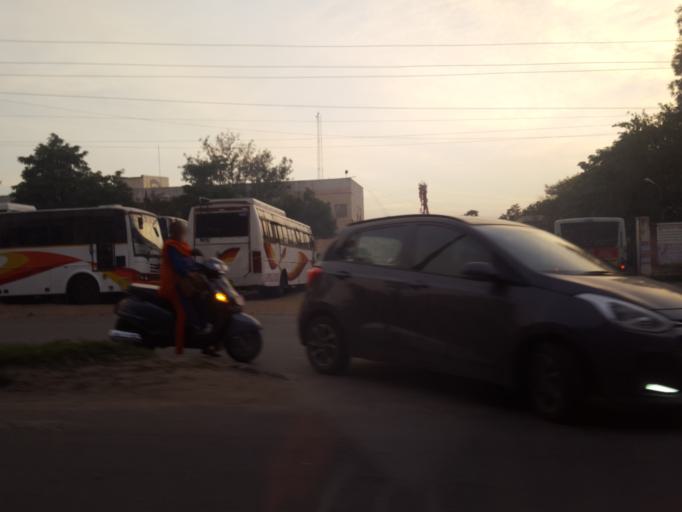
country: IN
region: Telangana
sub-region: Rangareddi
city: Kukatpalli
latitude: 17.5130
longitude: 78.3611
